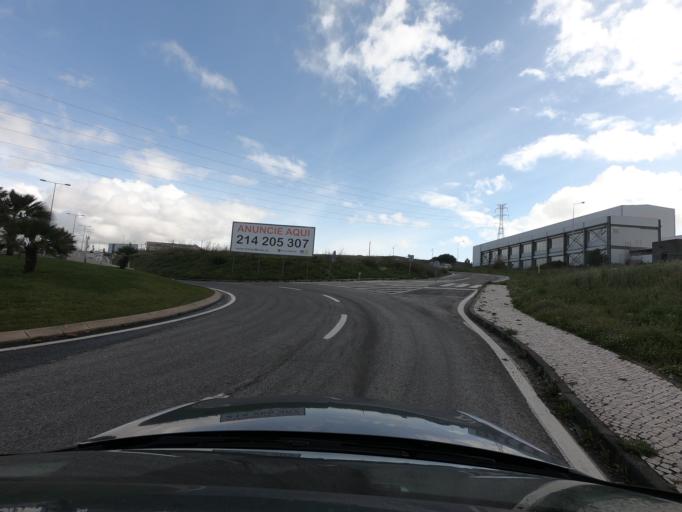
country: PT
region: Lisbon
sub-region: Sintra
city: Cacem
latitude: 38.7558
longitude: -9.3068
